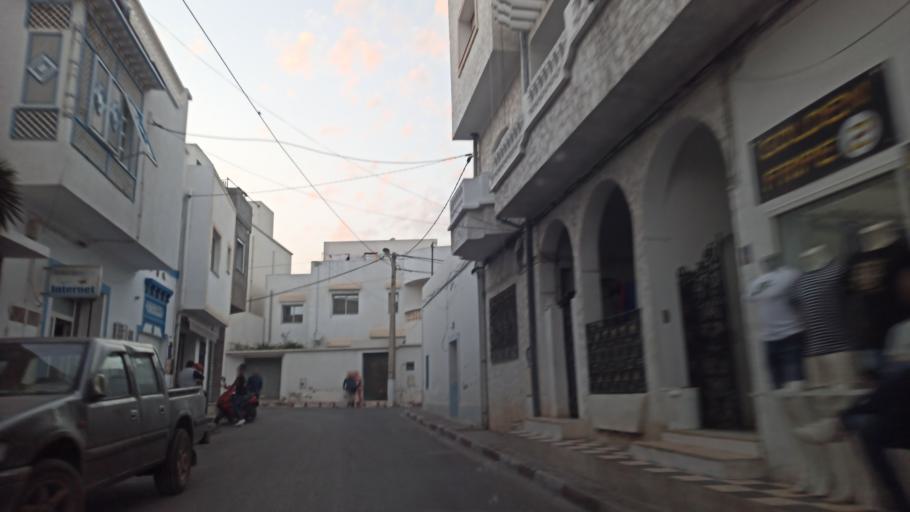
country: TN
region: Nabul
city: Al Hammamat
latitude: 36.4033
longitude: 10.6215
